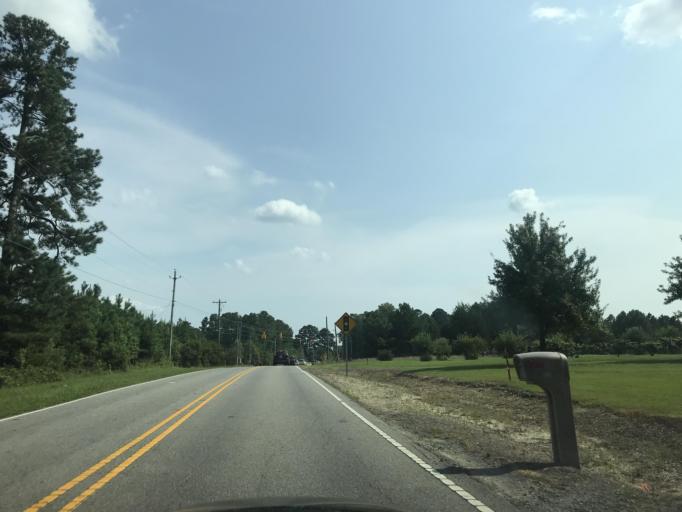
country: US
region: North Carolina
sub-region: Wake County
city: Morrisville
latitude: 35.8340
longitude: -78.8618
